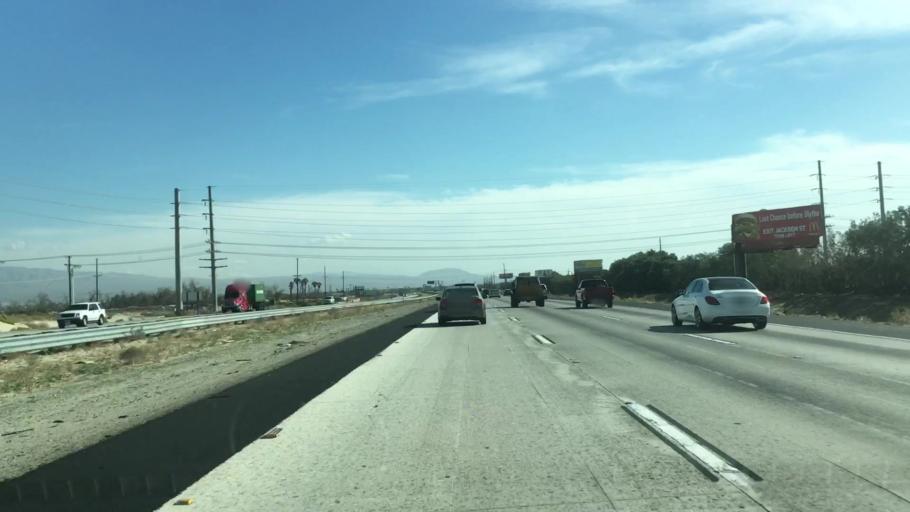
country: US
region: California
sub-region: Riverside County
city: Bermuda Dunes
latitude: 33.7421
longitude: -116.2567
